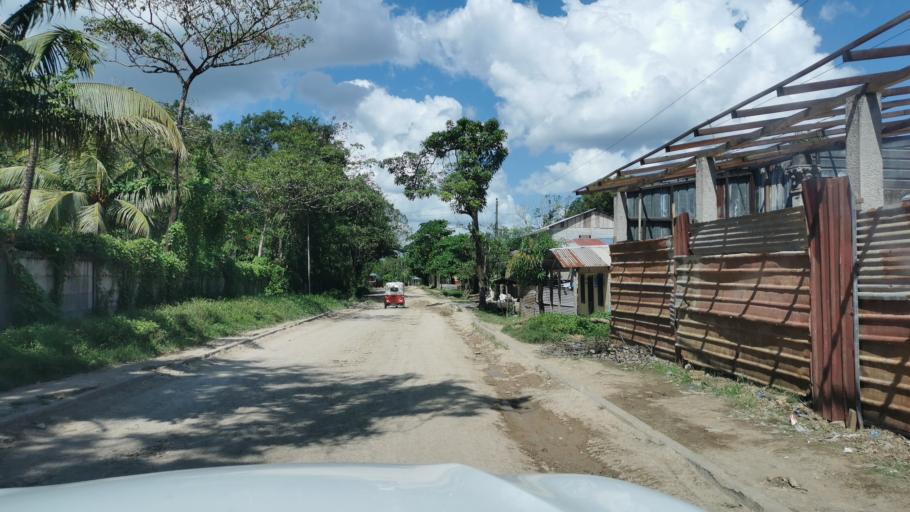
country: NI
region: Atlantico Sur
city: Rama
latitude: 12.1657
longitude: -84.2172
